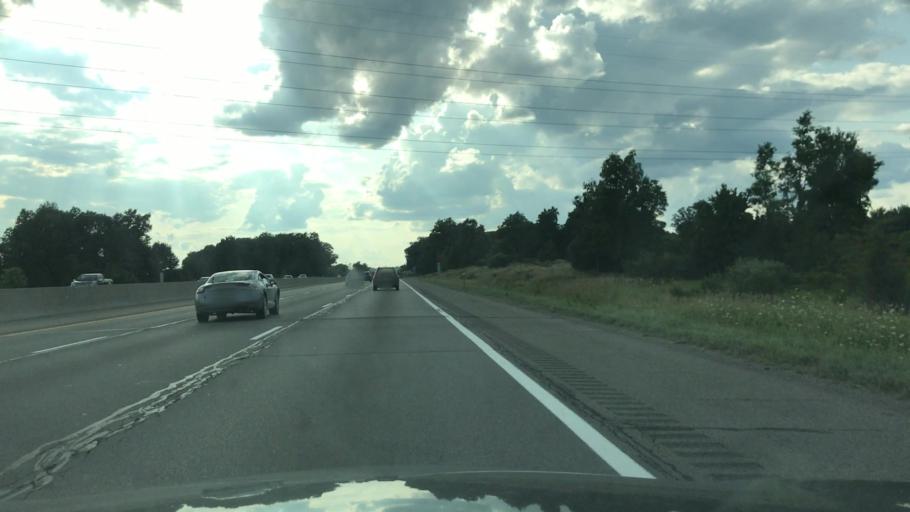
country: US
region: Michigan
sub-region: Oakland County
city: Wixom
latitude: 42.5107
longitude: -83.5850
